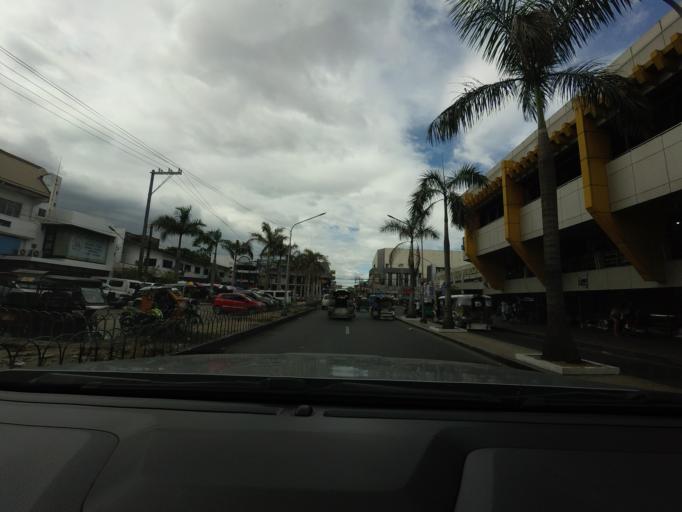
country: PH
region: Calabarzon
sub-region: Province of Rizal
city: Pateros
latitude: 14.5591
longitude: 121.0833
